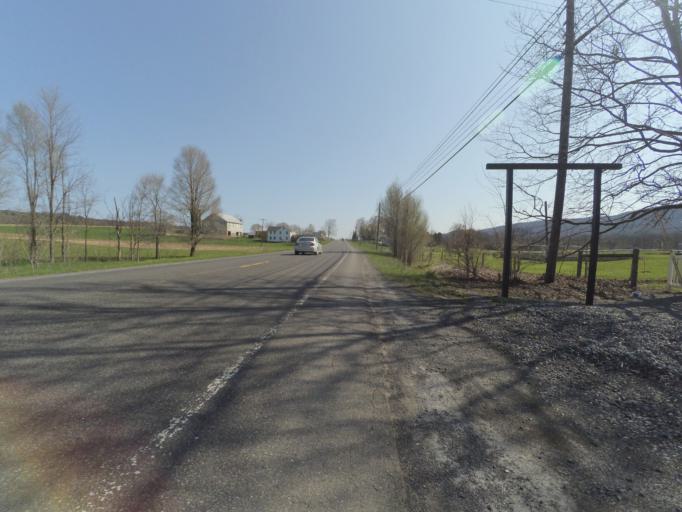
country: US
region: Pennsylvania
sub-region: Centre County
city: Zion
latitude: 40.9514
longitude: -77.6254
